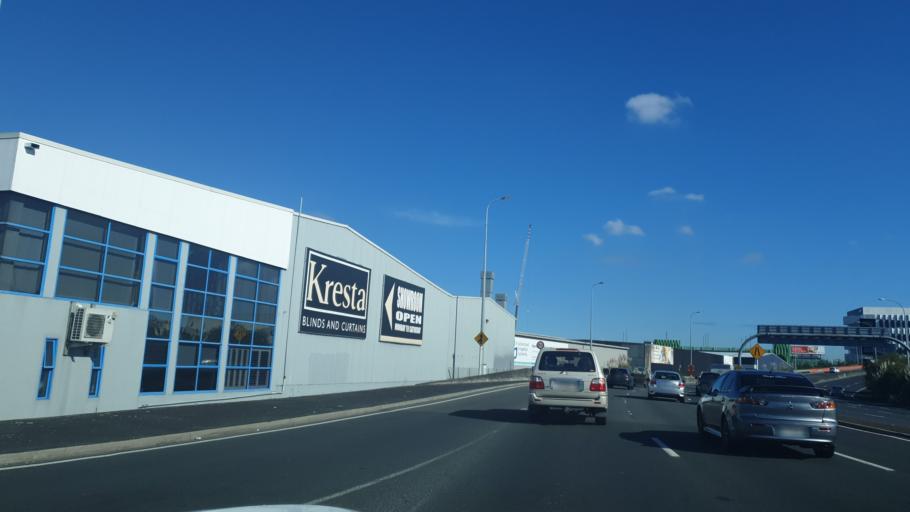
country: NZ
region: Auckland
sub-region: Auckland
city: Tamaki
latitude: -36.9153
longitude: 174.8462
